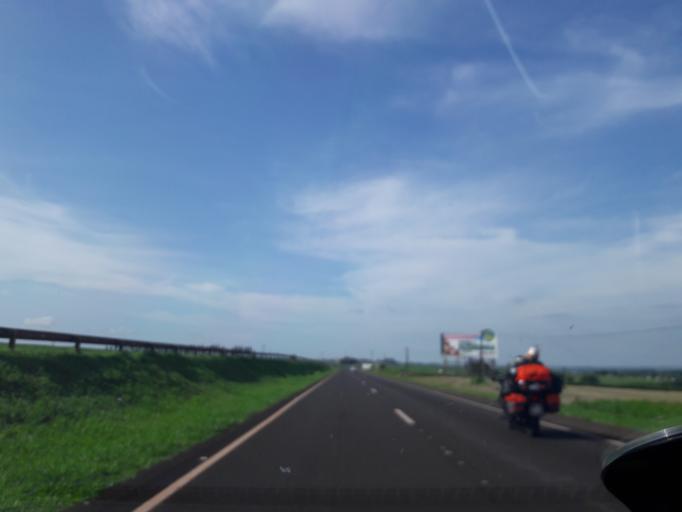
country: BR
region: Parana
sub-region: Paicandu
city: Paicandu
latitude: -23.5840
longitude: -52.0719
